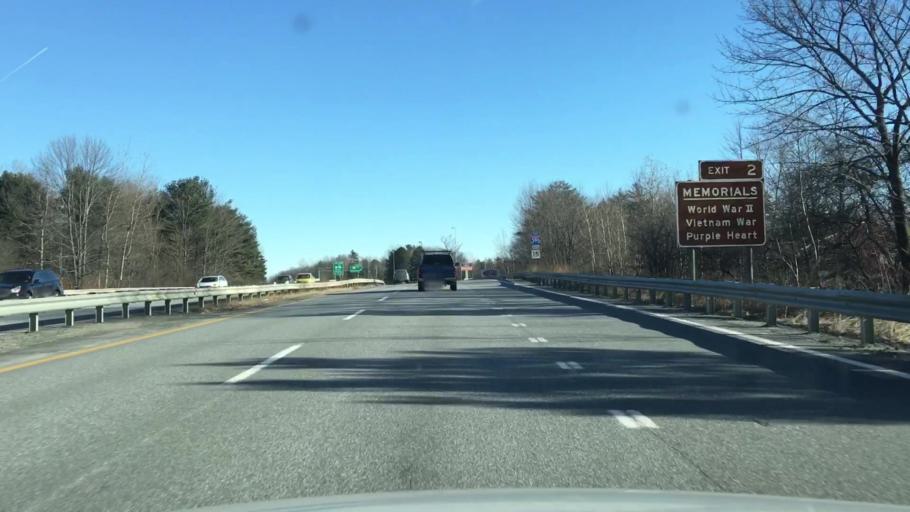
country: US
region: Maine
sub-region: Penobscot County
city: Bangor
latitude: 44.7863
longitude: -68.8025
